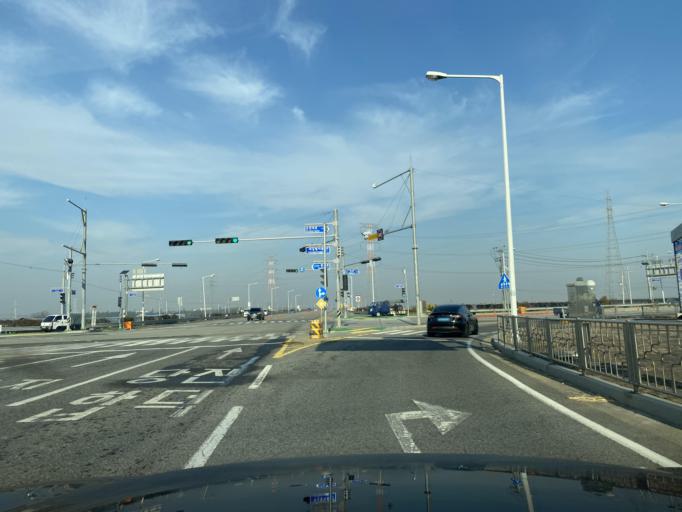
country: KR
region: Chungcheongnam-do
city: Yesan
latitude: 36.7387
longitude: 126.8591
